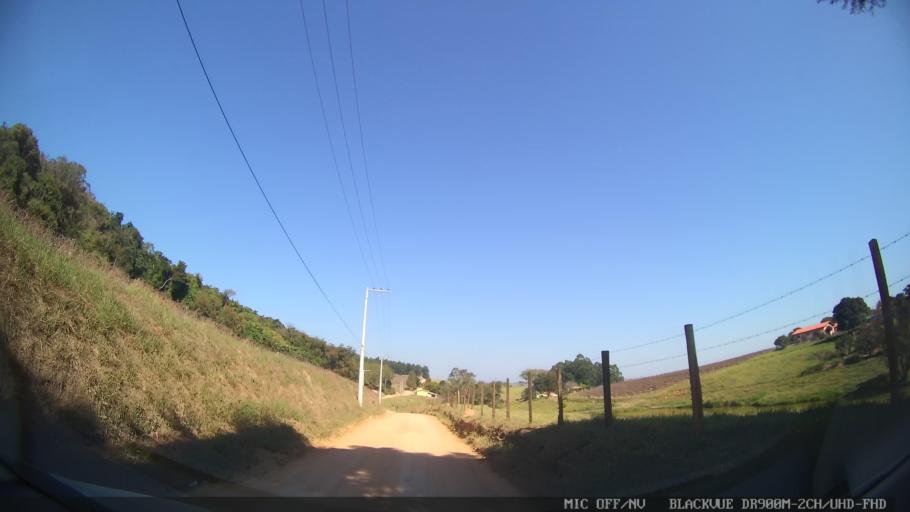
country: BR
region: Sao Paulo
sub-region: Itupeva
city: Itupeva
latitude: -23.1165
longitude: -47.0638
